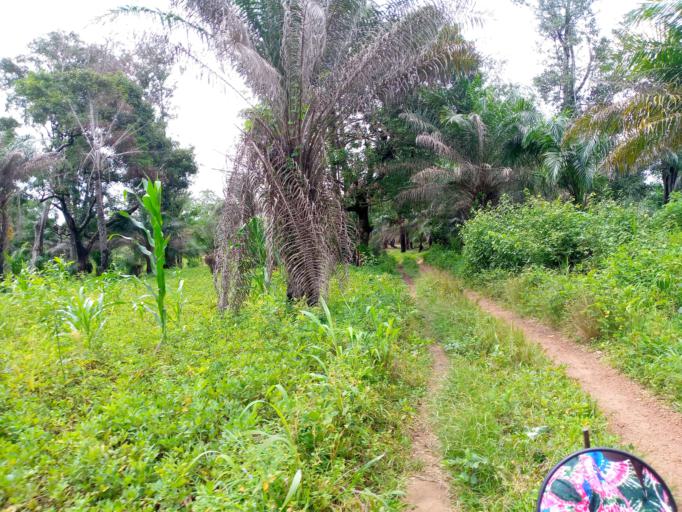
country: SL
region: Northern Province
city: Magburaka
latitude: 8.7263
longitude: -11.9326
